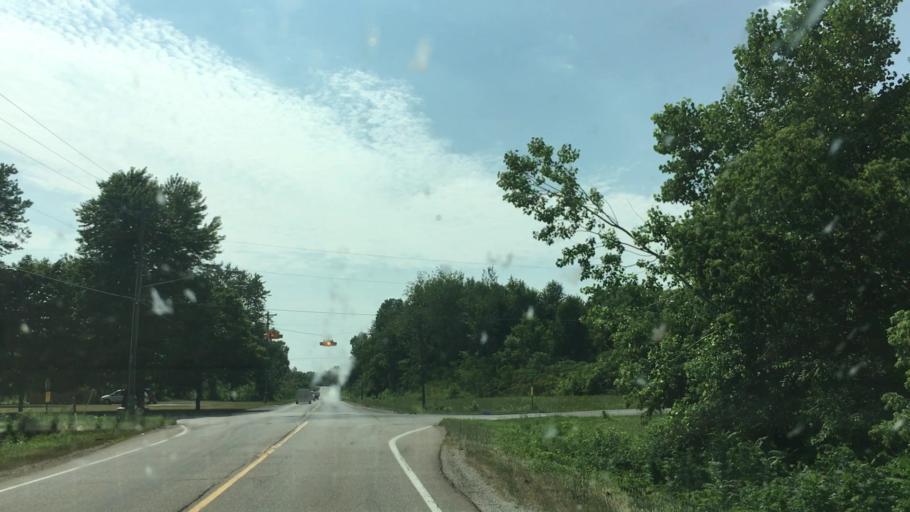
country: US
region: Michigan
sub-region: Kent County
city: Byron Center
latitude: 42.7827
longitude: -85.6824
